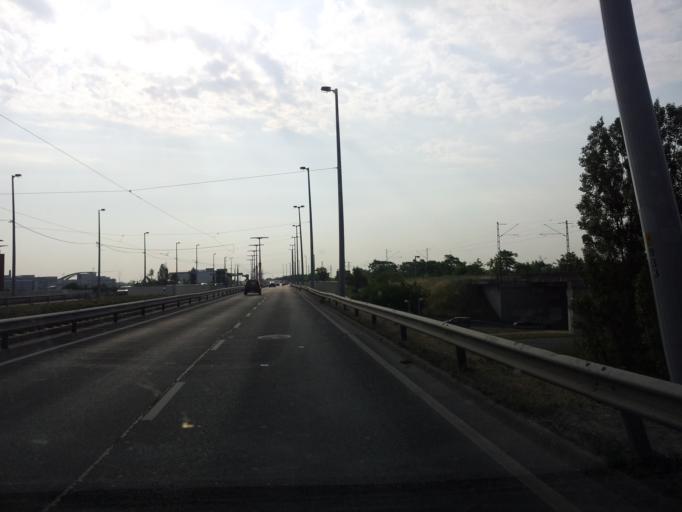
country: HU
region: Budapest
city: Budapest IX. keruelet
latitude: 47.4692
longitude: 19.0583
